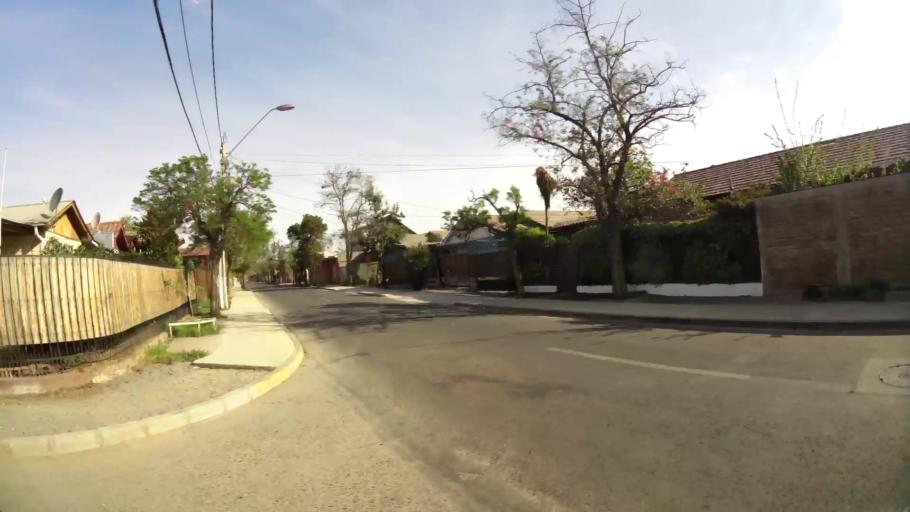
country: CL
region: Santiago Metropolitan
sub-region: Provincia de Santiago
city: Santiago
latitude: -33.5146
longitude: -70.6341
